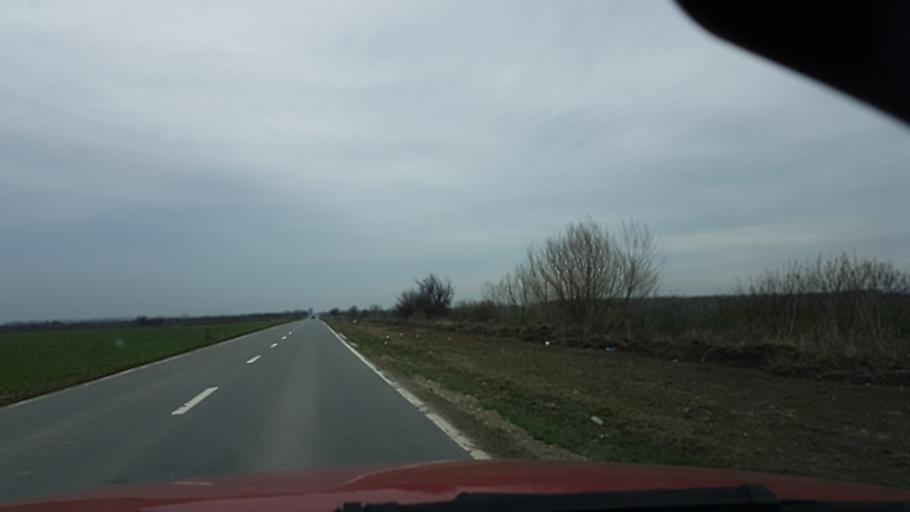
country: RO
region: Ilfov
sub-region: Comuna Tunari
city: Tunari
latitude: 44.5755
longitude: 26.1397
